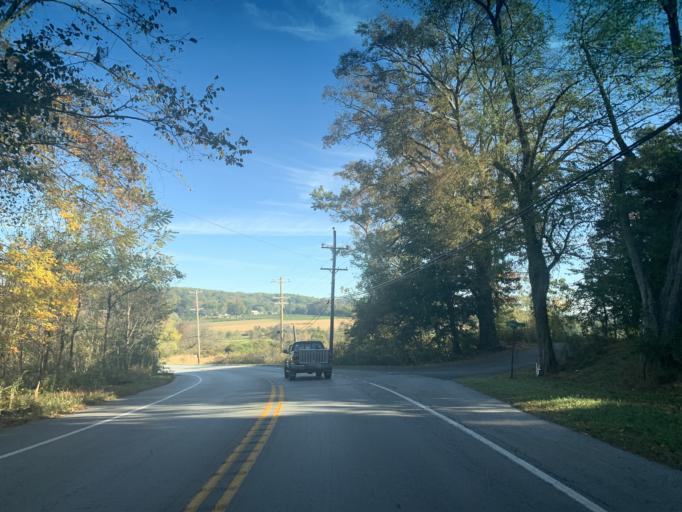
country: US
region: Pennsylvania
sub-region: Chester County
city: Parkesburg
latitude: 39.9525
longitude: -75.9112
